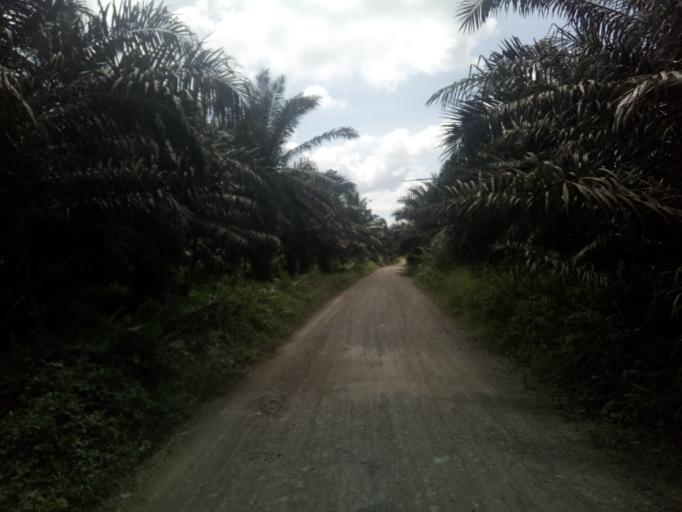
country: PH
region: Caraga
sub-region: Province of Agusan del Sur
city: Santa Josefa
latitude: 8.0262
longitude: 126.0160
